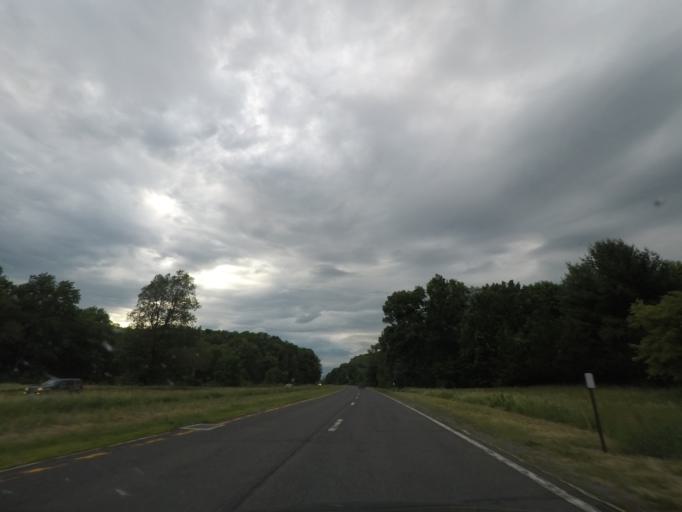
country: US
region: New York
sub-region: Dutchess County
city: Pine Plains
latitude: 42.0012
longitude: -73.7369
